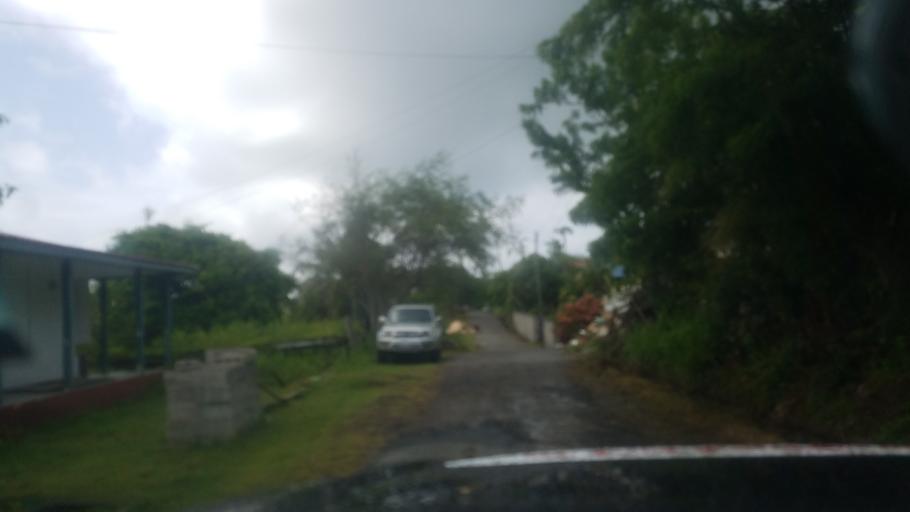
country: LC
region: Laborie Quarter
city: Laborie
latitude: 13.7468
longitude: -60.9589
